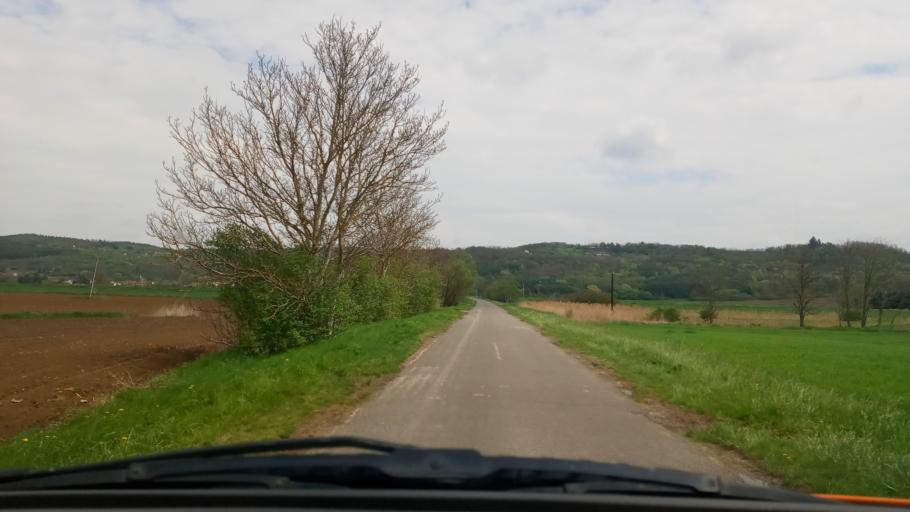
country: HU
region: Baranya
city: Sasd
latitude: 46.2586
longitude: 18.1101
